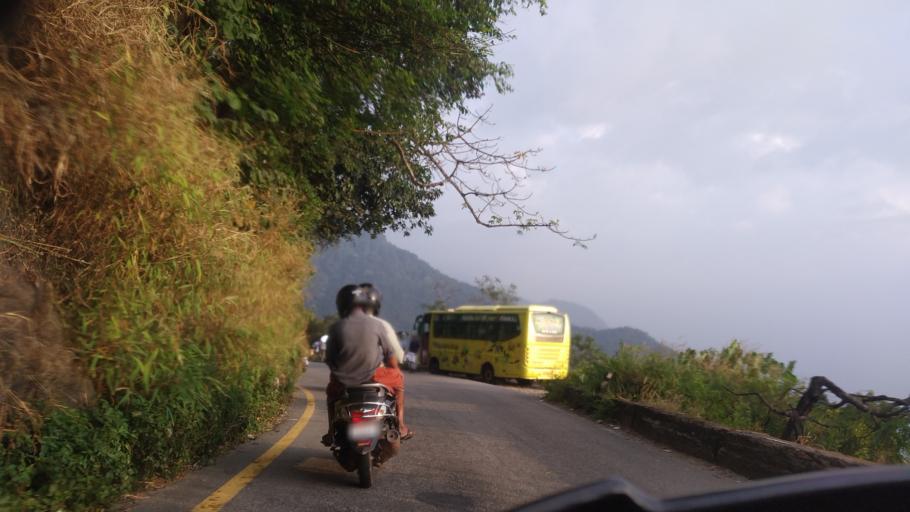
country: IN
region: Kerala
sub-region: Wayanad
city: Kalpetta
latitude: 11.5104
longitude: 76.0177
